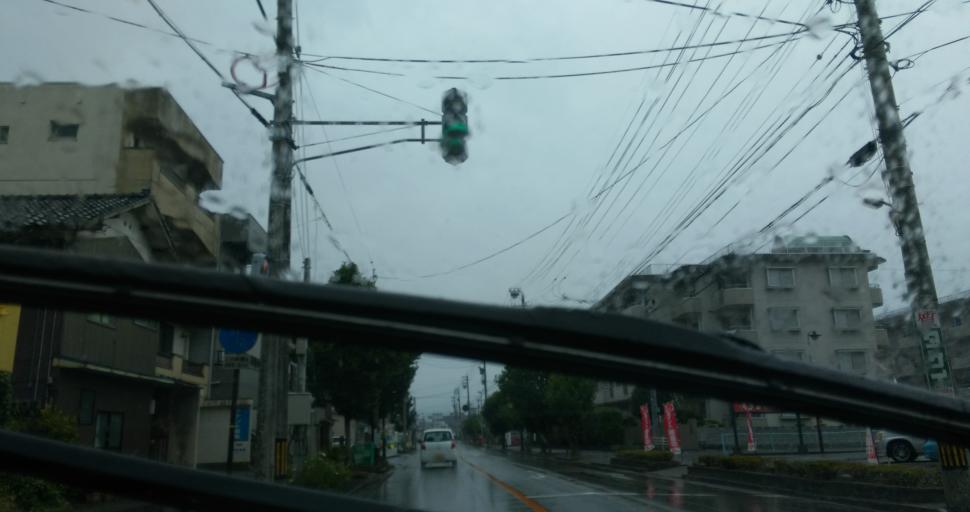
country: JP
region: Fukui
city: Fukui-shi
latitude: 36.0617
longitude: 136.2036
